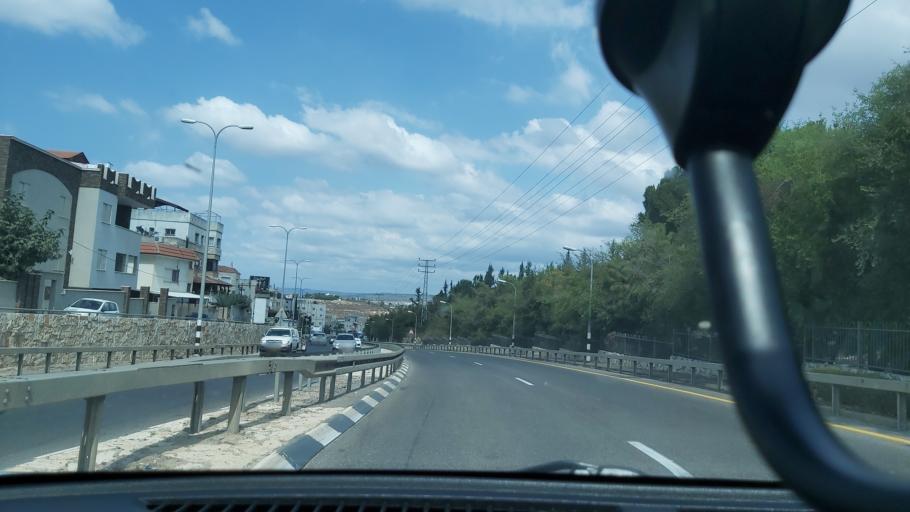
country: IL
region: Northern District
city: Judeida Makr
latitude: 32.9268
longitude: 35.1603
